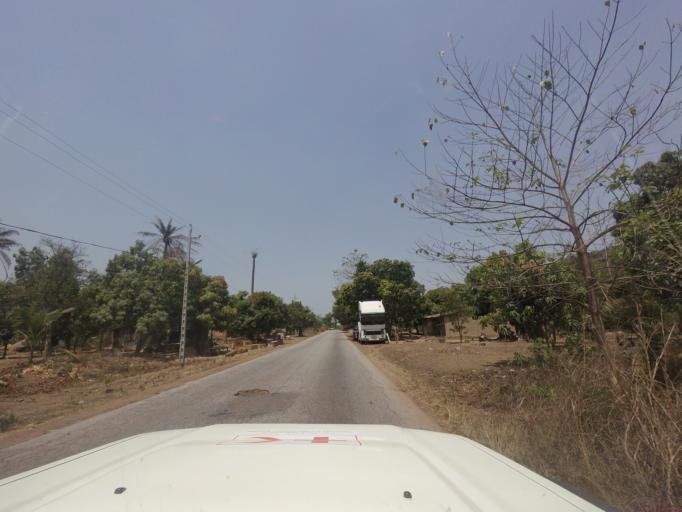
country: GN
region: Kindia
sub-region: Kindia
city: Kindia
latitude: 9.8652
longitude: -13.0649
